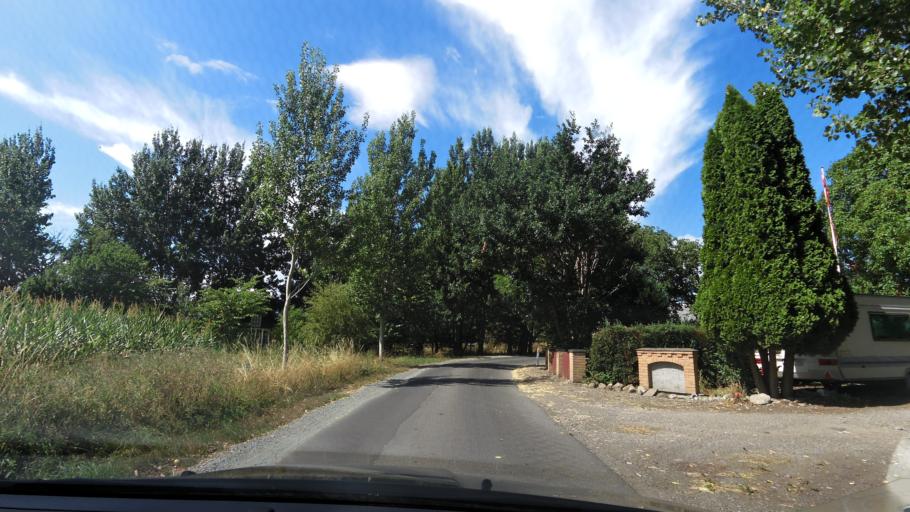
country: DK
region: South Denmark
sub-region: Nordfyns Kommune
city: Otterup
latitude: 55.5468
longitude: 10.4599
